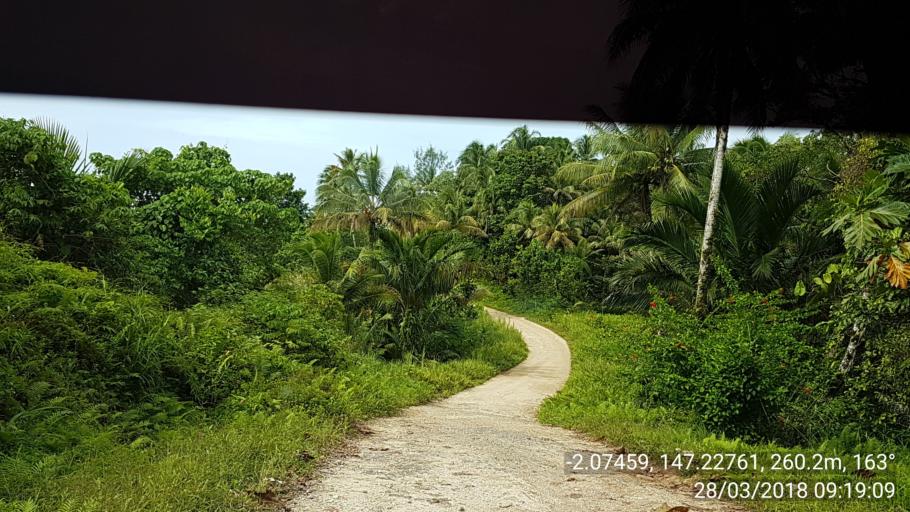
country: PG
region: Manus
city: Lorengau
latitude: -2.0746
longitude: 147.2276
